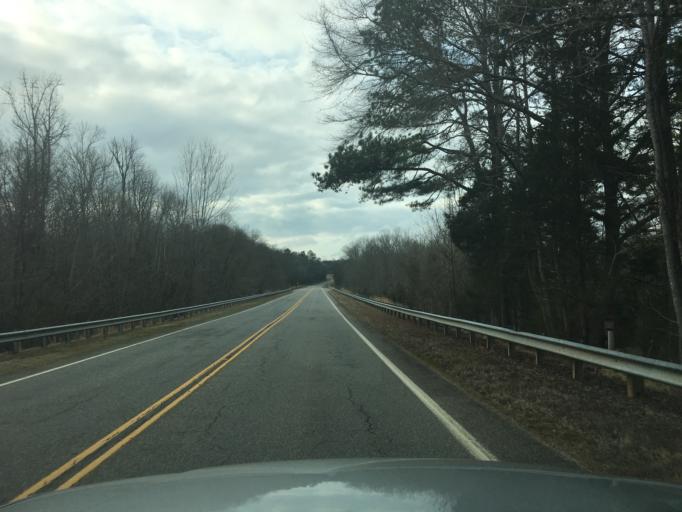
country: US
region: South Carolina
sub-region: Abbeville County
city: Due West
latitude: 34.2867
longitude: -82.4393
